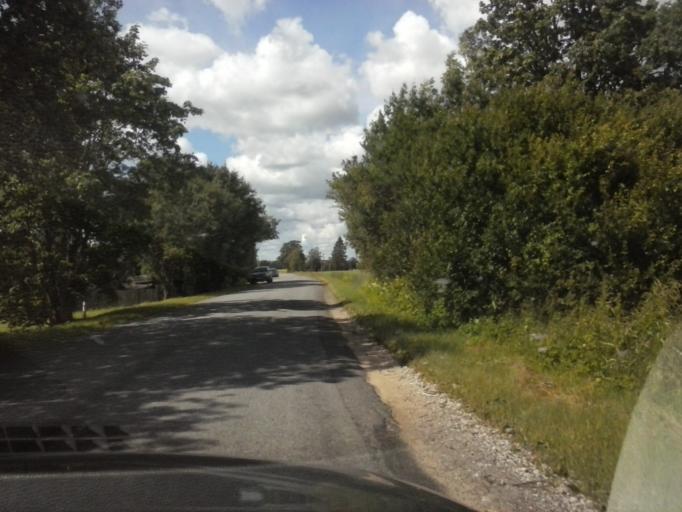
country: EE
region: Laeaene-Virumaa
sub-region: Vaeike-Maarja vald
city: Vaike-Maarja
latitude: 59.0576
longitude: 26.3394
